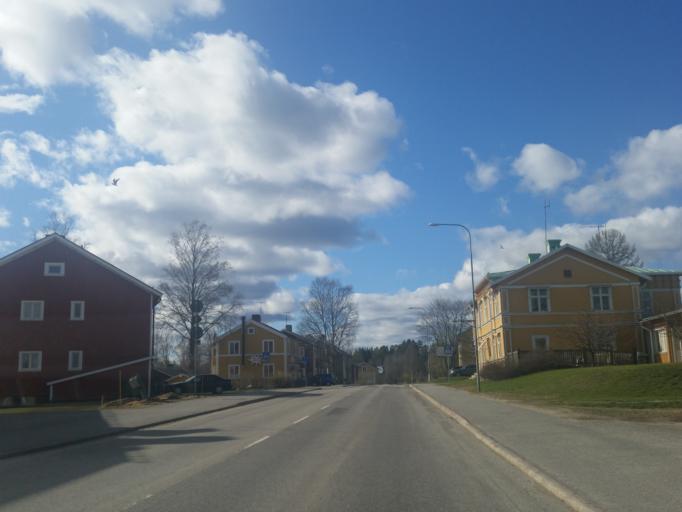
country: SE
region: Vaesterbotten
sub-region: Robertsfors Kommun
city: Robertsfors
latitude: 64.1943
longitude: 20.8459
